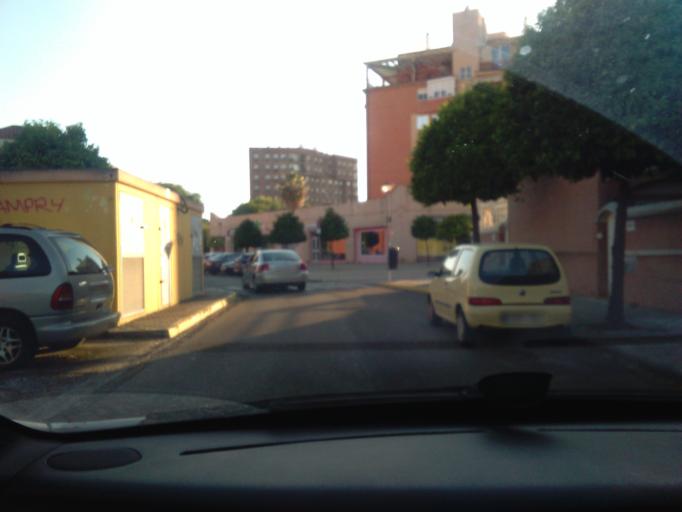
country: ES
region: Andalusia
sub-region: Provincia de Sevilla
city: Sevilla
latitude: 37.4046
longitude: -5.9439
